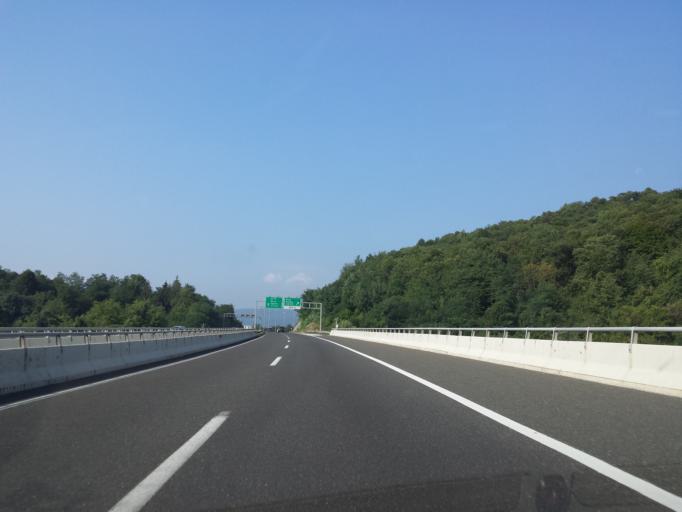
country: HR
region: Karlovacka
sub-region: Grad Ogulin
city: Ogulin
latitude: 45.4139
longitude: 15.2804
